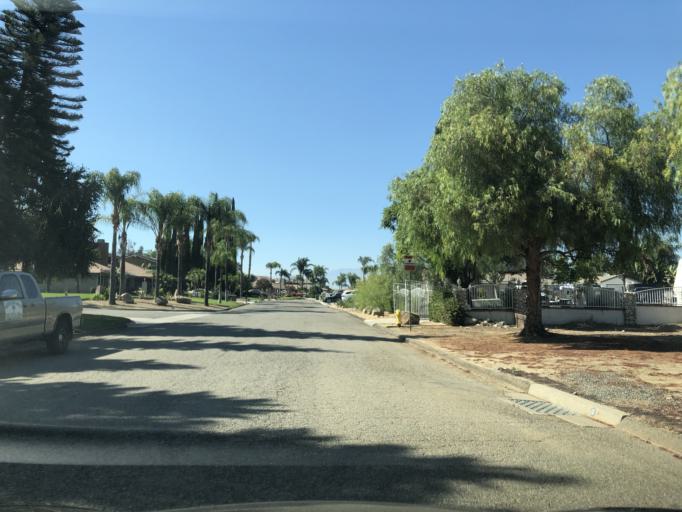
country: US
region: California
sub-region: Riverside County
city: El Cerrito
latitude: 33.8589
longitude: -117.5334
